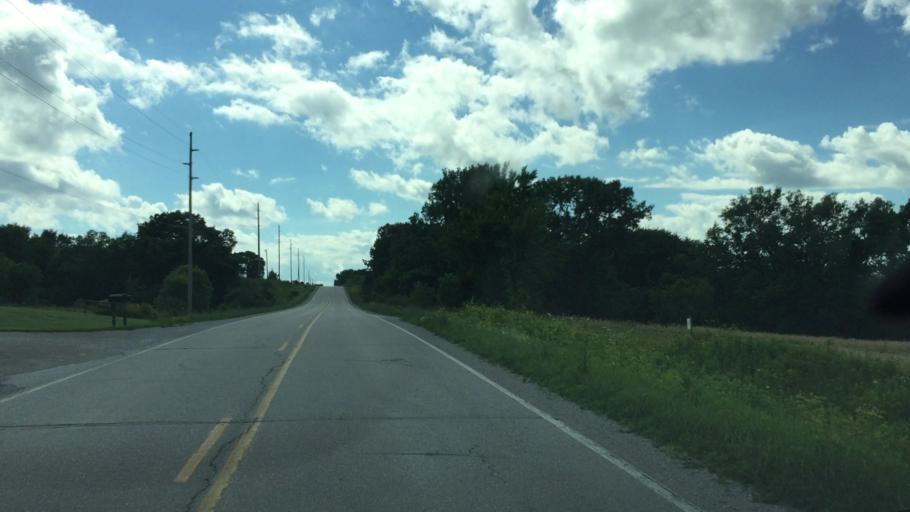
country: US
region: Iowa
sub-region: Linn County
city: Ely
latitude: 41.8474
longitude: -91.6000
